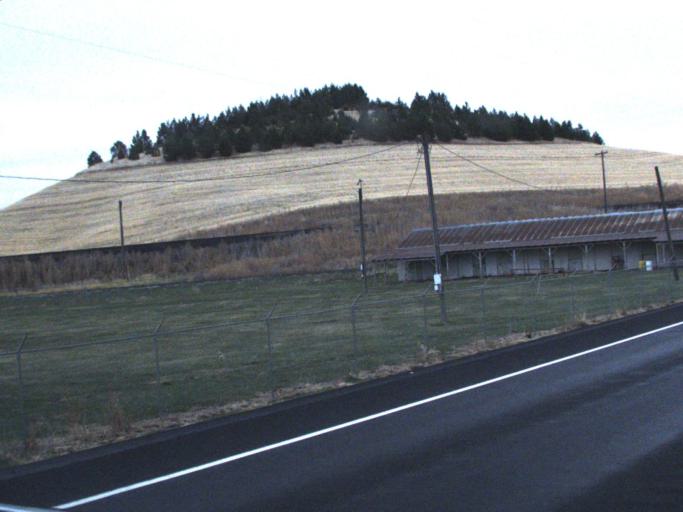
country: US
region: Washington
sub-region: Whitman County
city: Colfax
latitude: 46.8648
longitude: -117.4304
